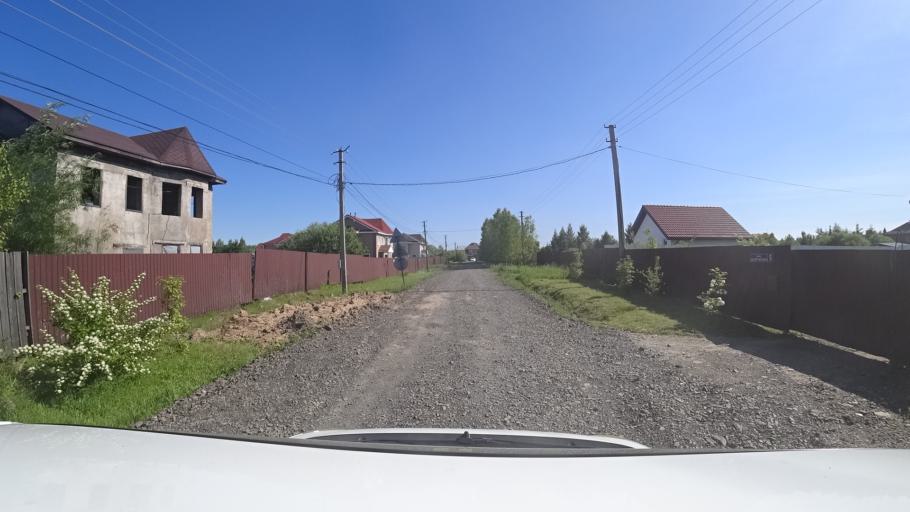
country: RU
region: Khabarovsk Krai
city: Topolevo
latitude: 48.5515
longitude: 135.1726
